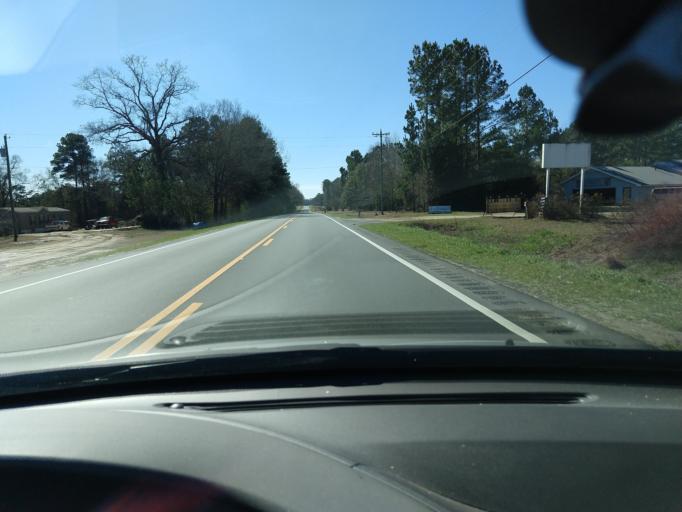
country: US
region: Alabama
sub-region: Covington County
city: Andalusia
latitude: 31.2677
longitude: -86.5120
